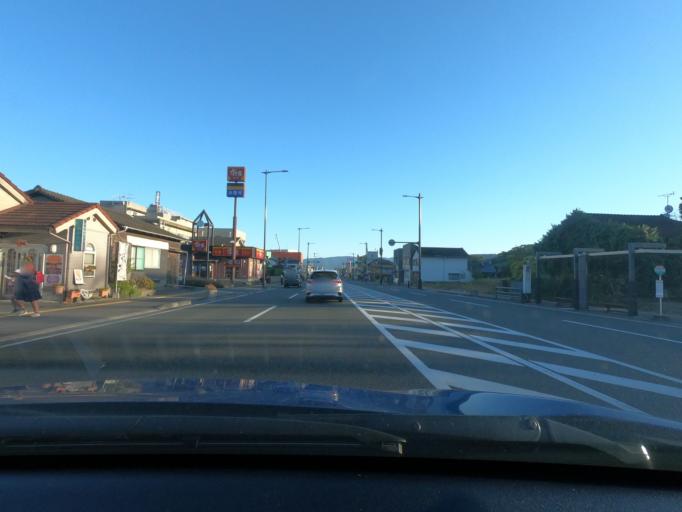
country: JP
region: Kagoshima
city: Satsumasendai
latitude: 31.8308
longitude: 130.2958
